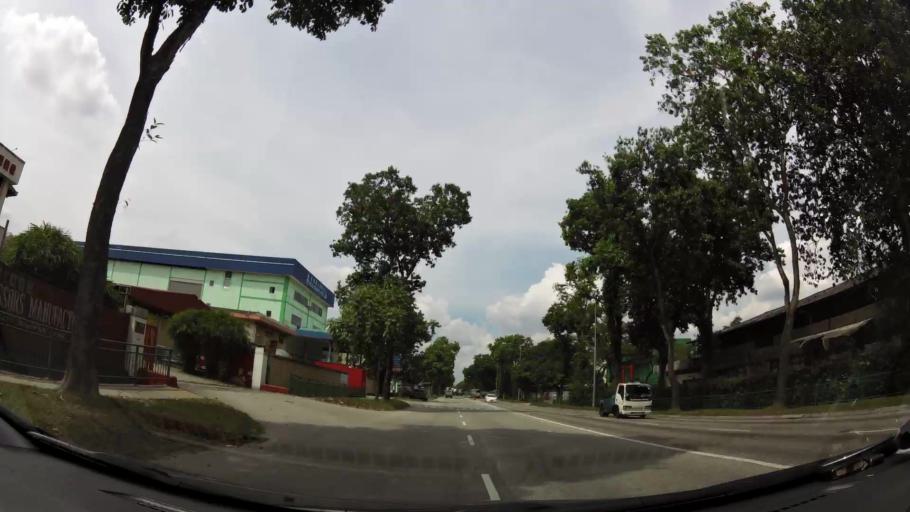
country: MY
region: Johor
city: Johor Bahru
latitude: 1.4156
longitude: 103.7514
